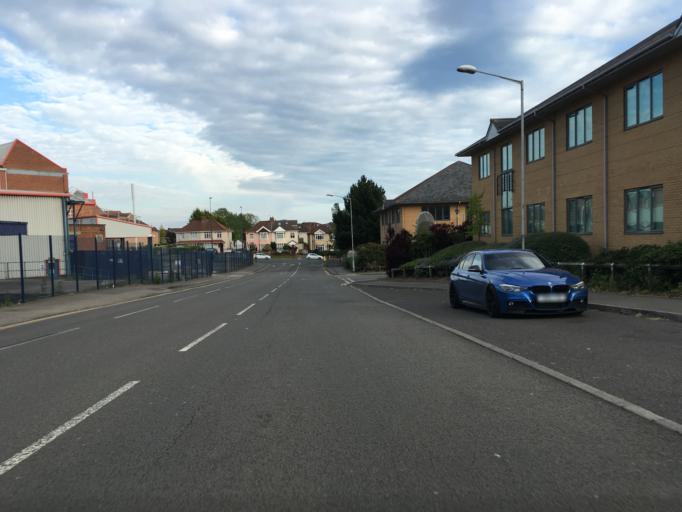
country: GB
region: England
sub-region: South Gloucestershire
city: Stoke Gifford
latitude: 51.5093
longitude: -2.5797
